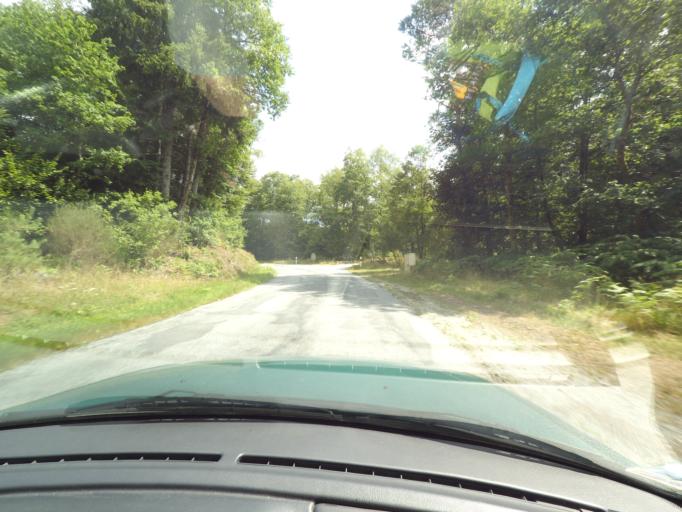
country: FR
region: Limousin
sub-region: Departement de la Correze
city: Bugeat
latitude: 45.7346
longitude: 1.8962
